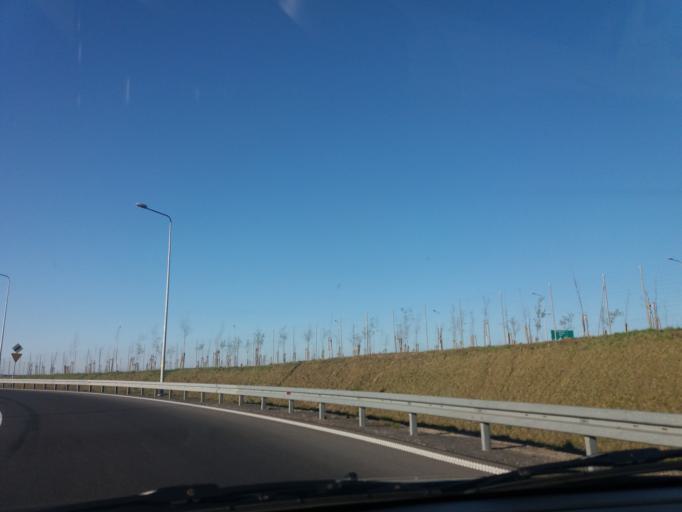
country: PL
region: Warmian-Masurian Voivodeship
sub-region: Powiat nidzicki
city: Nidzica
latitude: 53.3330
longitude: 20.4391
